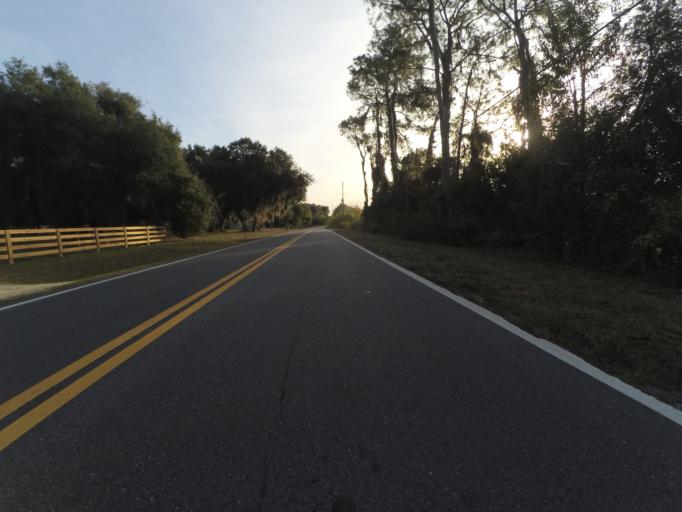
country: US
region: Florida
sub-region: Lake County
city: Umatilla
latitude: 28.9311
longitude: -81.6812
